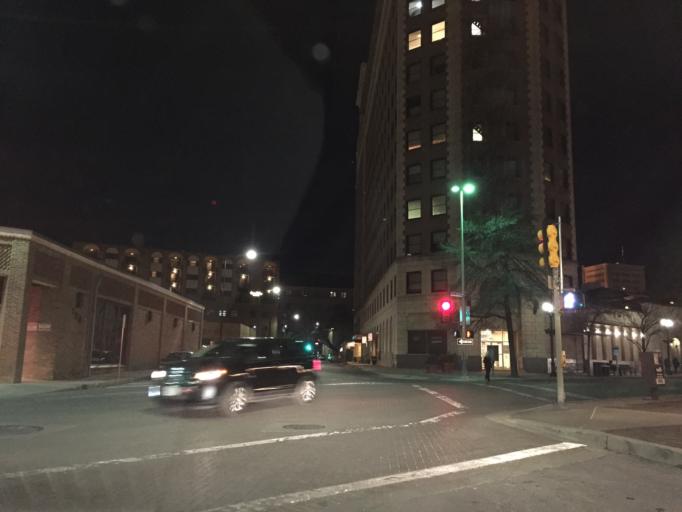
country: US
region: Texas
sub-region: Bexar County
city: San Antonio
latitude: 29.4226
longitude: -98.4915
